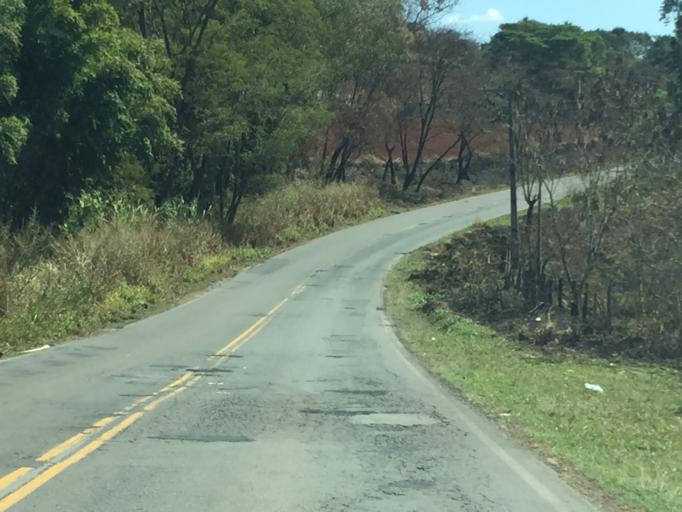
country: BR
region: Sao Paulo
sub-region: Moji-Guacu
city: Mogi-Gaucu
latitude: -22.3492
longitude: -46.8760
